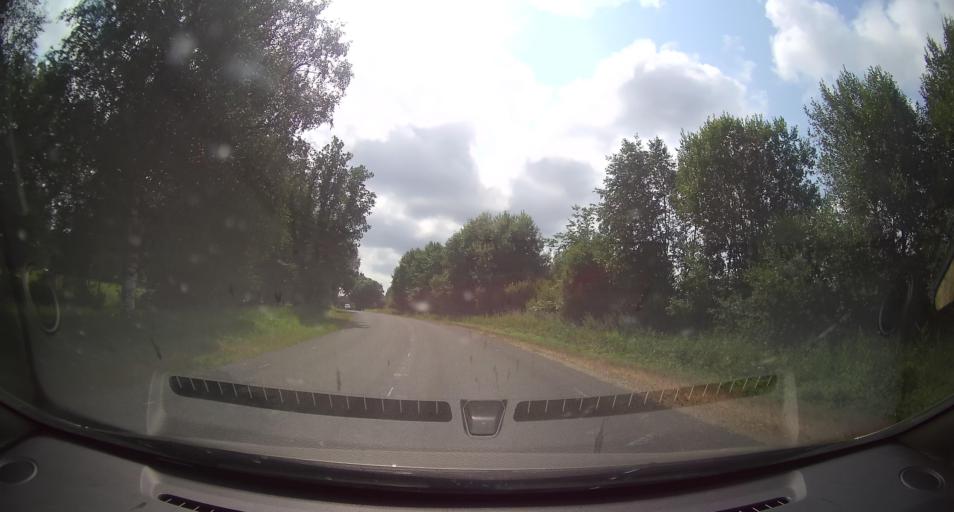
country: EE
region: Paernumaa
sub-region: Audru vald
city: Audru
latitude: 58.4446
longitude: 24.3075
